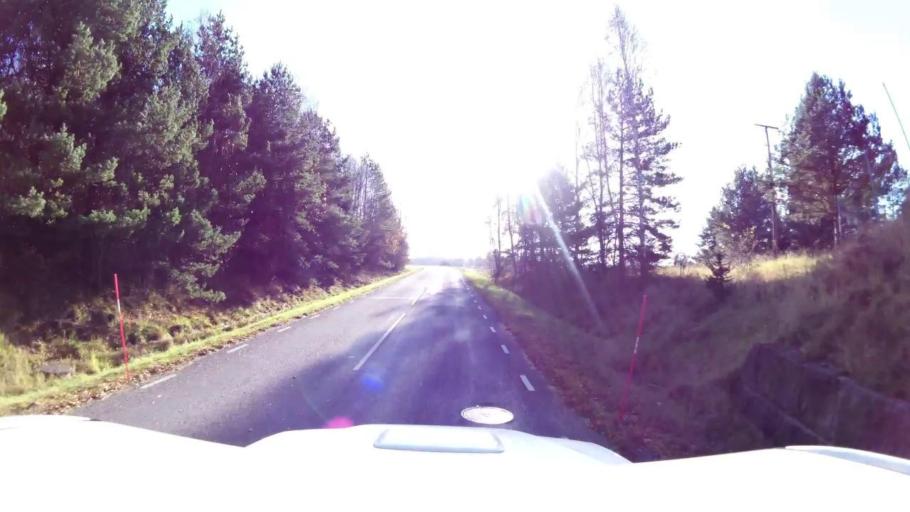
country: SE
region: OEstergoetland
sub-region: Linkopings Kommun
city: Linghem
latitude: 58.4551
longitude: 15.7754
